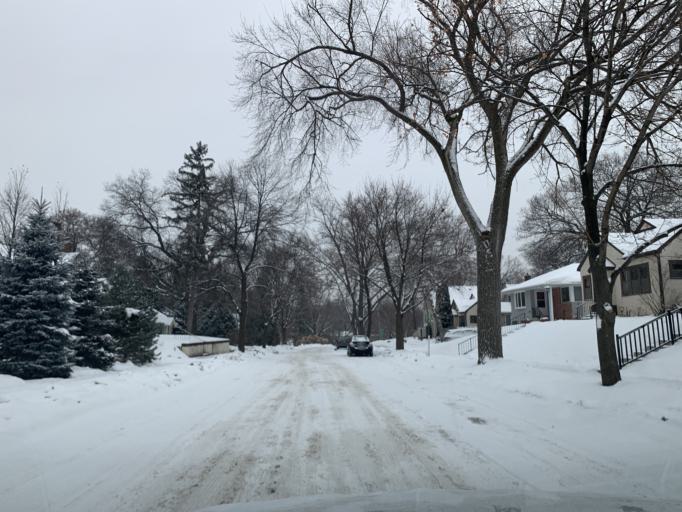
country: US
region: Minnesota
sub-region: Hennepin County
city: Saint Louis Park
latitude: 44.9494
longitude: -93.3391
